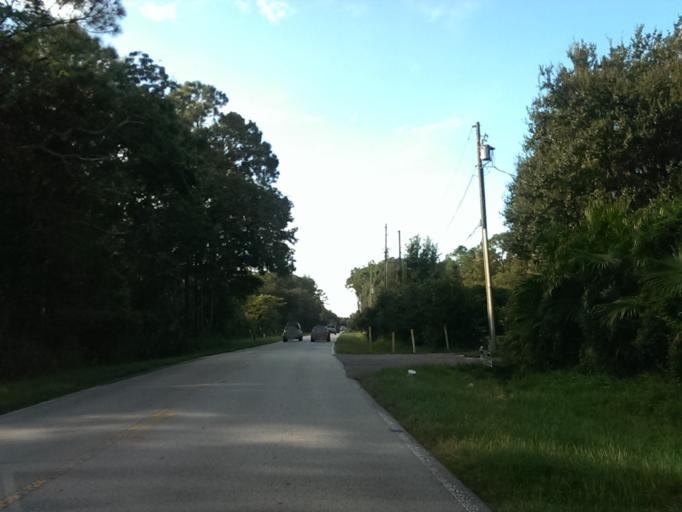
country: US
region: Florida
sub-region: Orange County
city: Lake Butler
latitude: 28.4558
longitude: -81.5961
